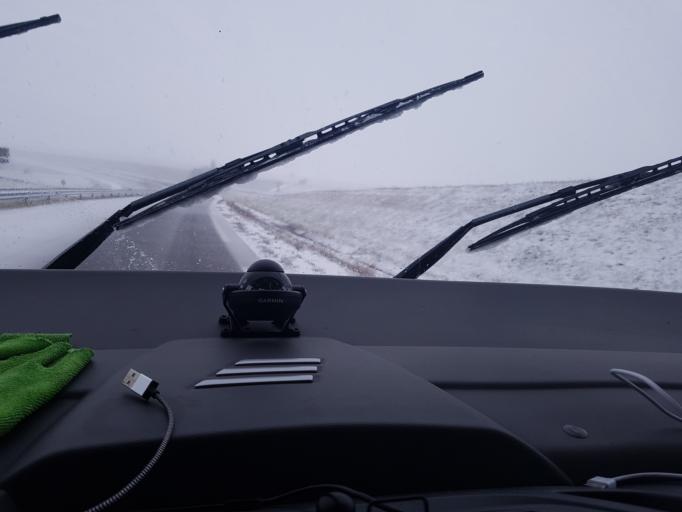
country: FR
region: Lorraine
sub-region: Departement de la Moselle
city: Chateau-Salins
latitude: 48.8467
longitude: 6.4566
